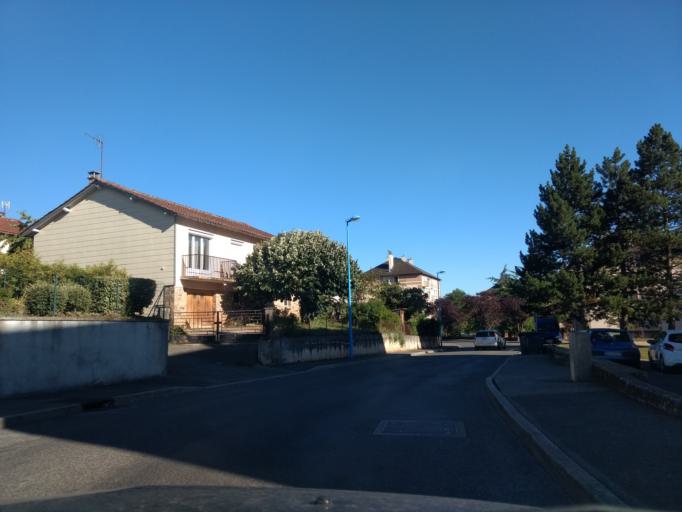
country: FR
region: Midi-Pyrenees
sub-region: Departement de l'Aveyron
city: Rodez
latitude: 44.3653
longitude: 2.6001
